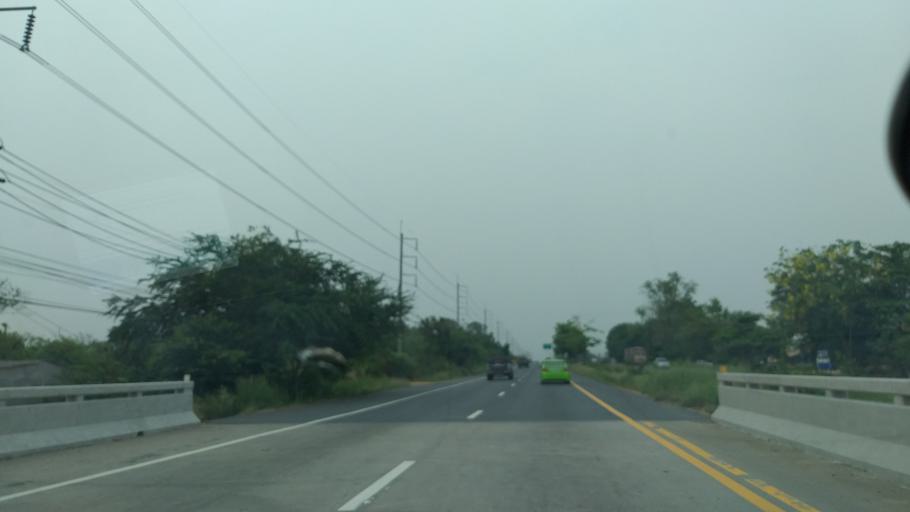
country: TH
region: Chon Buri
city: Ko Chan
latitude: 13.4114
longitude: 101.2821
